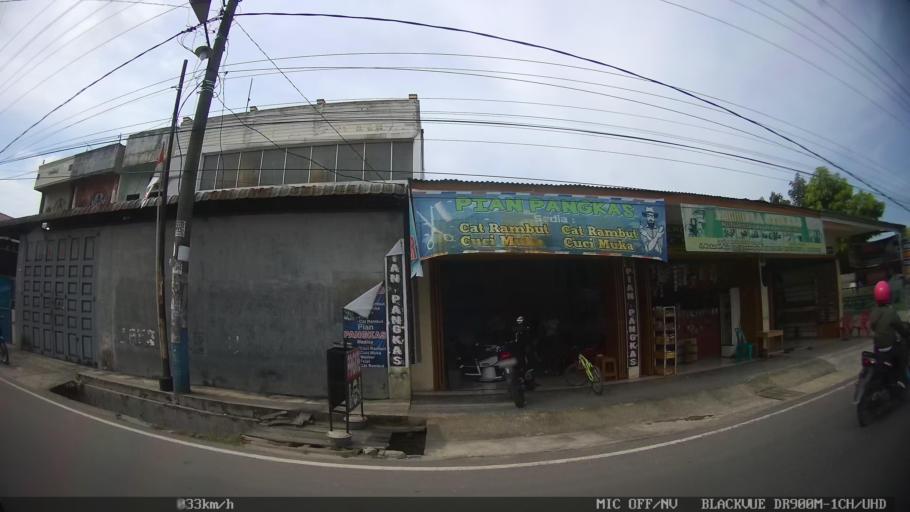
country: ID
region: North Sumatra
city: Medan
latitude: 3.6072
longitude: 98.7636
